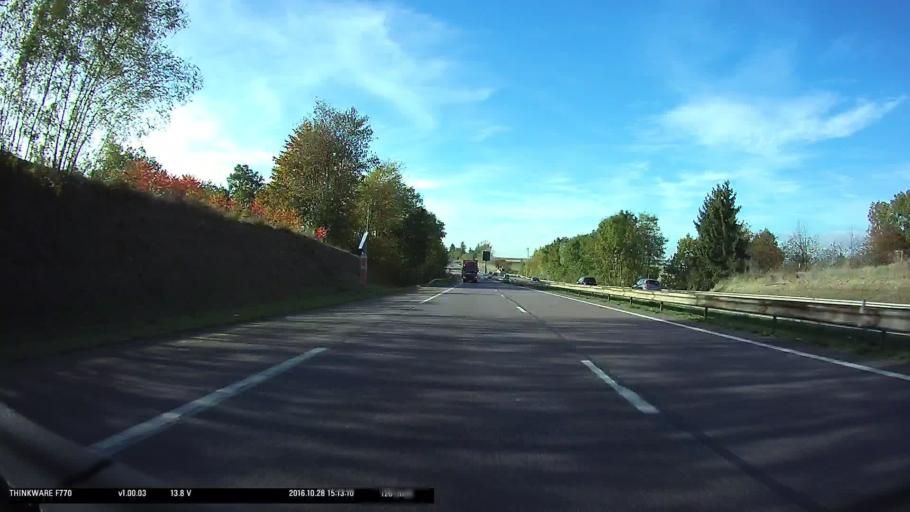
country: FR
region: Alsace
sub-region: Departement du Bas-Rhin
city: Mommenheim
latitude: 48.7676
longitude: 7.6470
